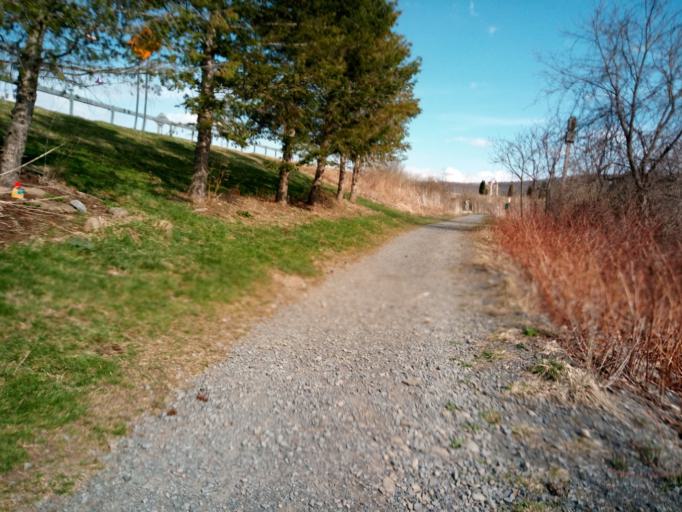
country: US
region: New York
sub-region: Chemung County
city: Big Flats
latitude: 42.1469
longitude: -76.9112
